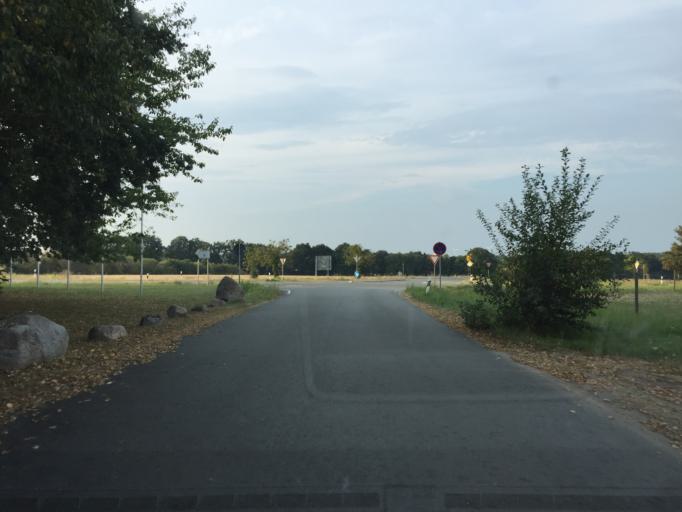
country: DE
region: Lower Saxony
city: Binnen
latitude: 52.6553
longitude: 9.1227
